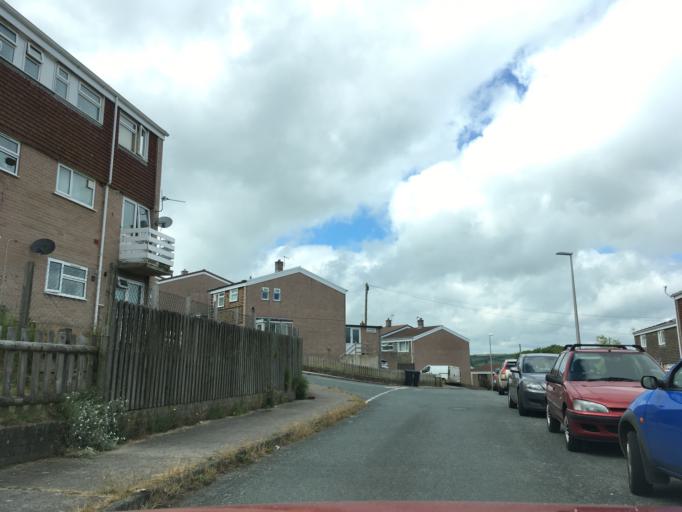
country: GB
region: England
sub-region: Devon
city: Dartmouth
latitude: 50.3524
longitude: -3.5971
